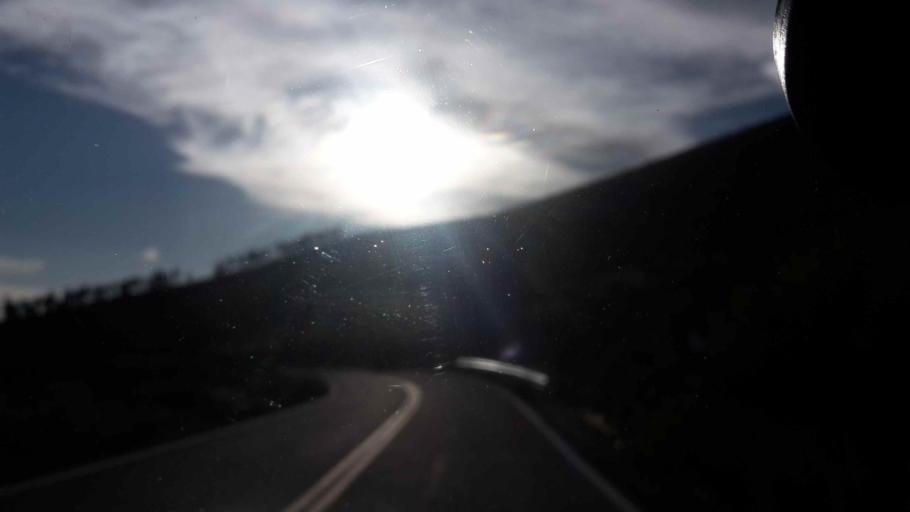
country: BO
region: Cochabamba
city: Arani
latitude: -17.5616
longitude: -65.7142
